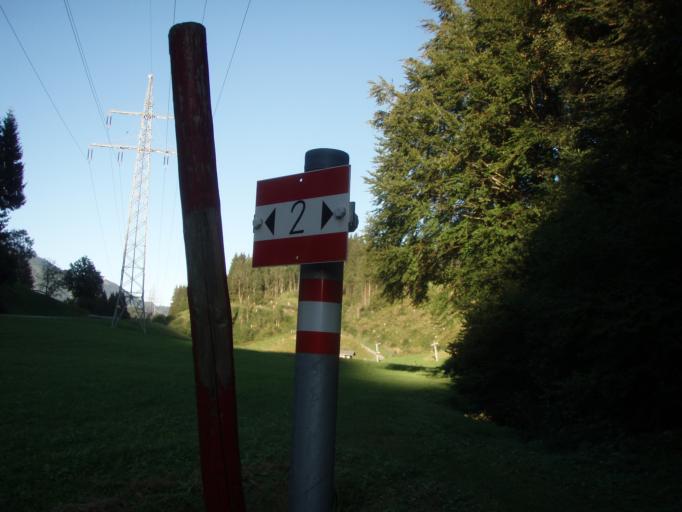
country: AT
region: Salzburg
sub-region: Politischer Bezirk Zell am See
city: Lend
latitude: 47.3180
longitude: 13.0603
